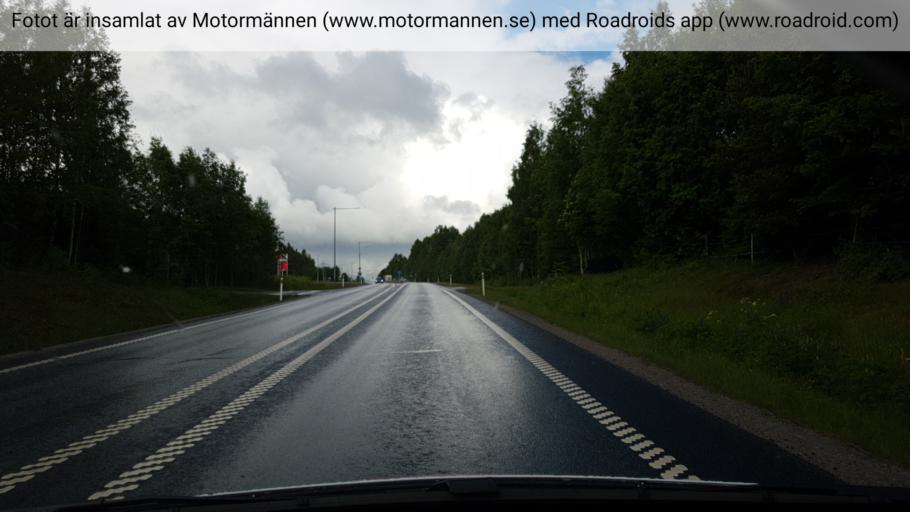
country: SE
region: Vaesterbotten
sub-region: Vannas Kommun
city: Vannasby
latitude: 63.9207
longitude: 19.8119
